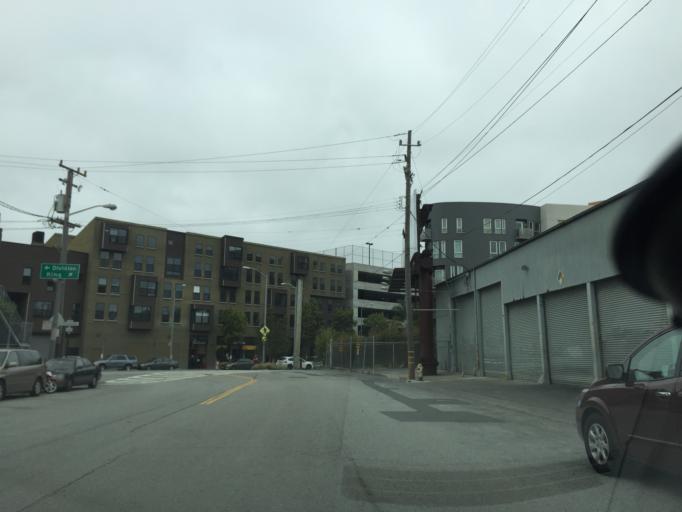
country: US
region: California
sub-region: San Francisco County
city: San Francisco
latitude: 37.7695
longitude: -122.4020
